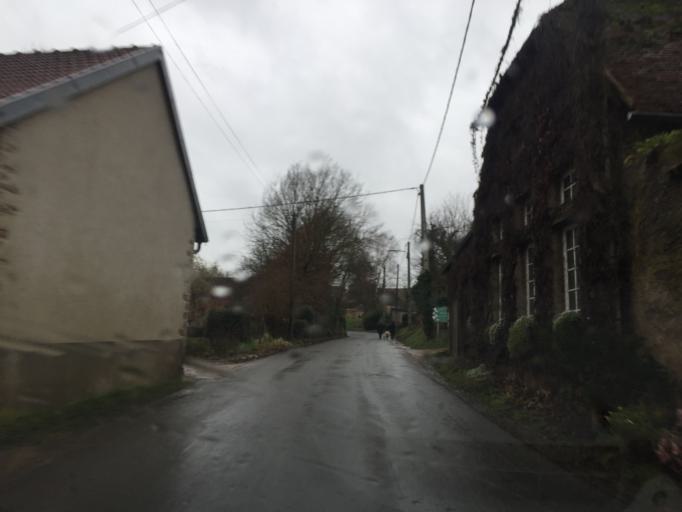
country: FR
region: Franche-Comte
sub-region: Departement du Jura
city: Dole
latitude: 47.1546
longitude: 5.4829
